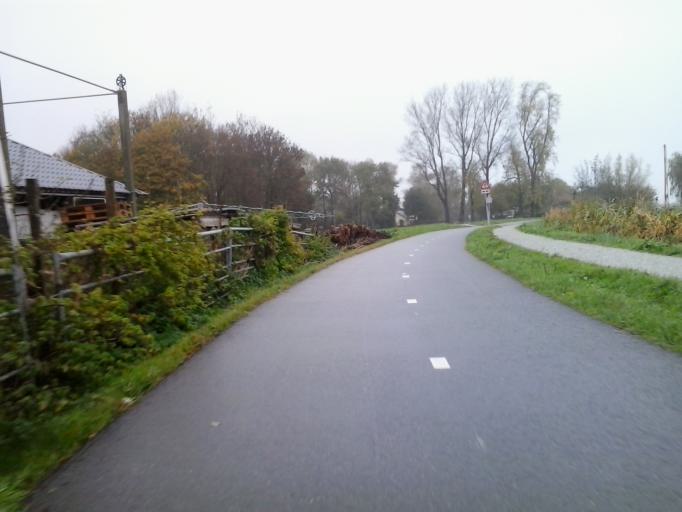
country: NL
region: South Holland
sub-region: Gemeente Lansingerland
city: Bleiswijk
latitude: 51.9975
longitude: 4.5492
